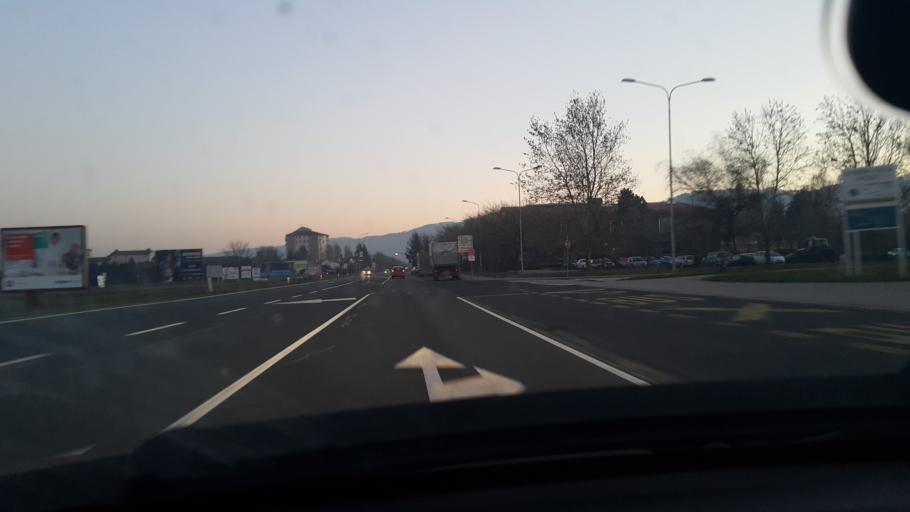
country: SI
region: Brezice
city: Brezice
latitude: 45.9078
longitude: 15.6015
